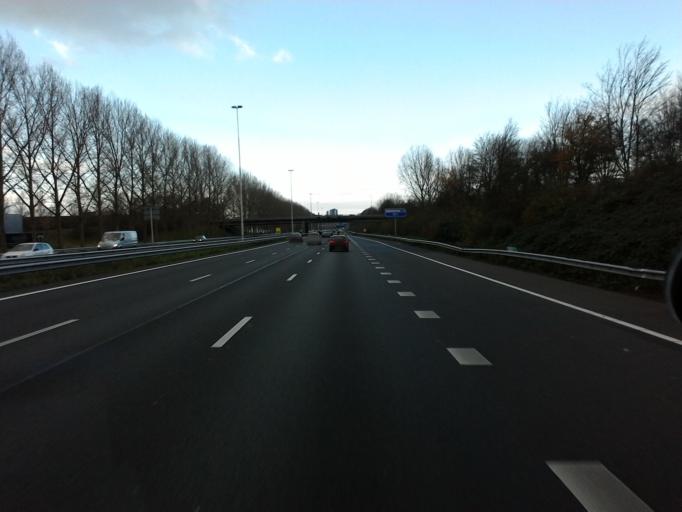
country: NL
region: South Holland
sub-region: Gemeente Capelle aan den IJssel
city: Capelle aan den IJssel
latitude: 51.9649
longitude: 4.5831
